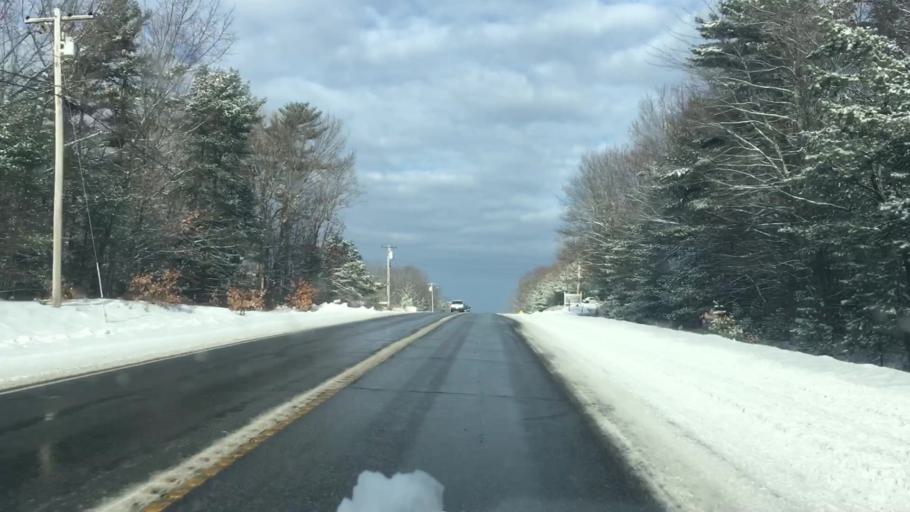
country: US
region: Maine
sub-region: Cumberland County
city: Raymond
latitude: 43.9179
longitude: -70.5230
